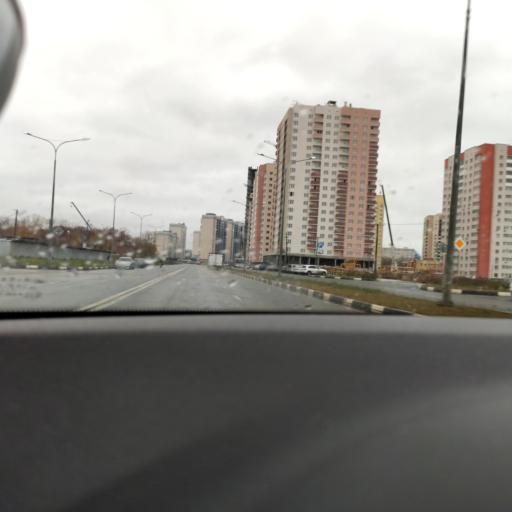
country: RU
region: Samara
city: Samara
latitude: 53.1447
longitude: 50.0765
